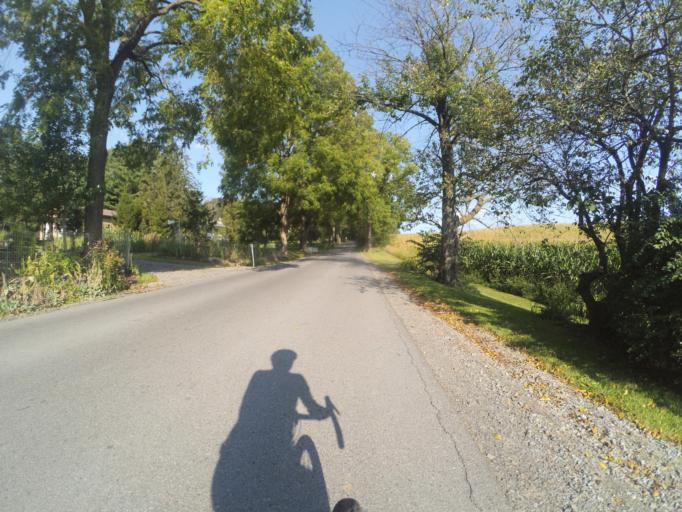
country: US
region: Pennsylvania
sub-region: Centre County
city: Boalsburg
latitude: 40.7993
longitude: -77.7835
